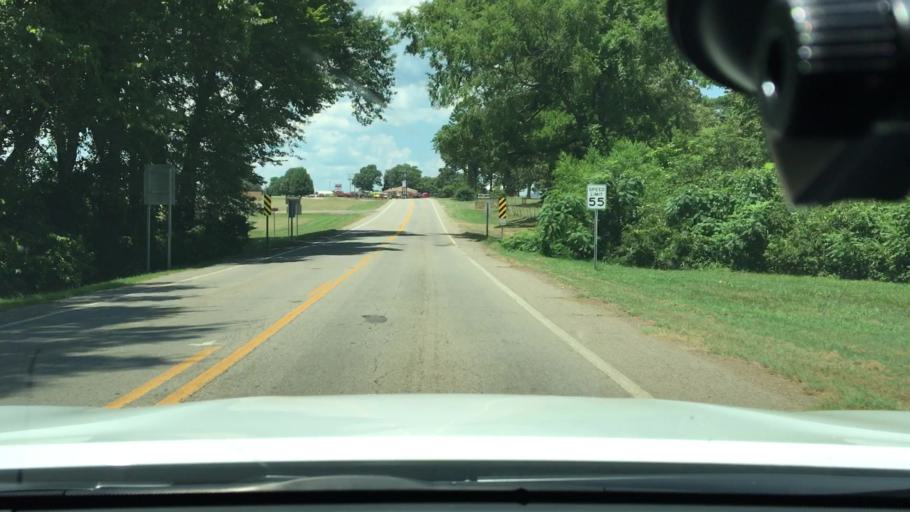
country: US
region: Arkansas
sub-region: Logan County
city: Booneville
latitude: 35.1507
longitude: -93.8187
